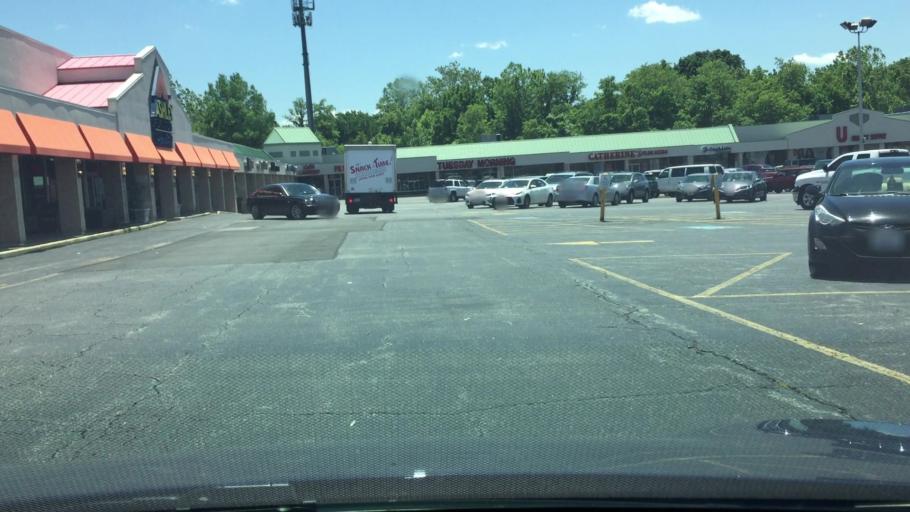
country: US
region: Virginia
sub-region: City of Lynchburg
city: West Lynchburg
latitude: 37.3735
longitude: -79.1829
